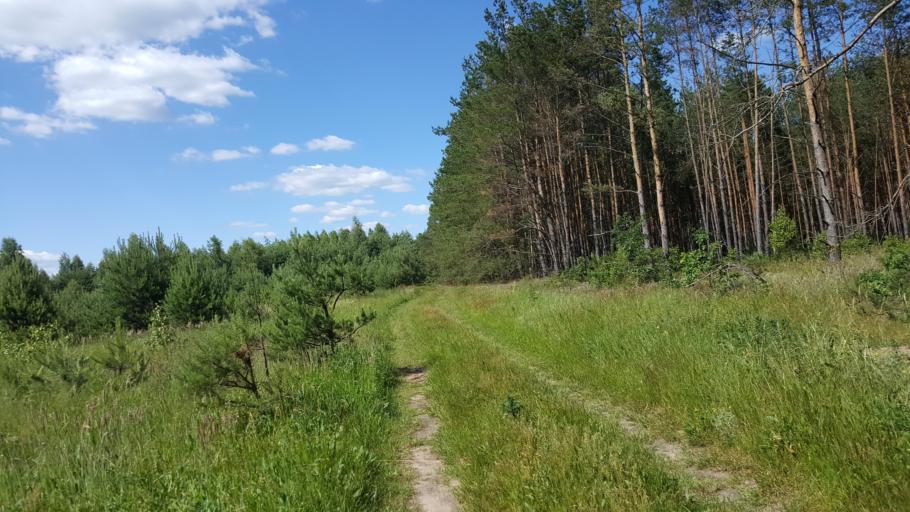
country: PL
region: Podlasie
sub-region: Powiat hajnowski
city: Hajnowka
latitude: 52.5618
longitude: 23.6022
